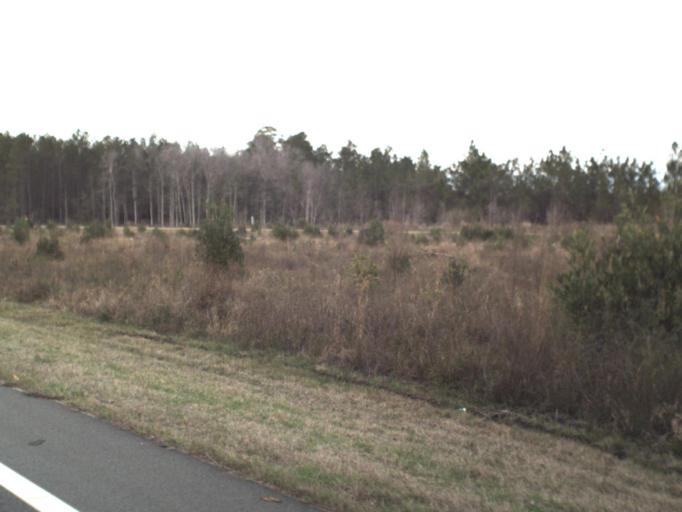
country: US
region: Florida
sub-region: Gulf County
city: Wewahitchka
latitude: 30.1302
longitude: -85.2309
